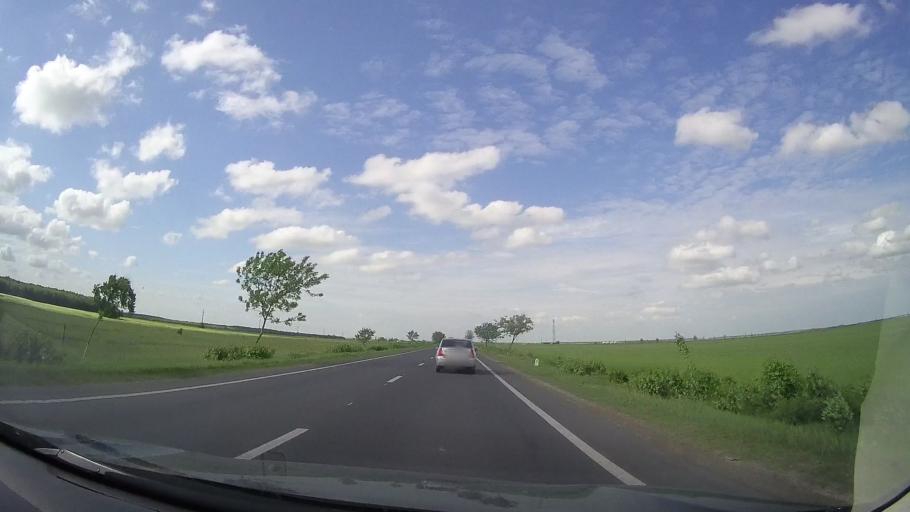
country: RO
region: Giurgiu
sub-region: Comuna Ghimpati
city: Ghimpati
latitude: 44.2190
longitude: 25.8028
